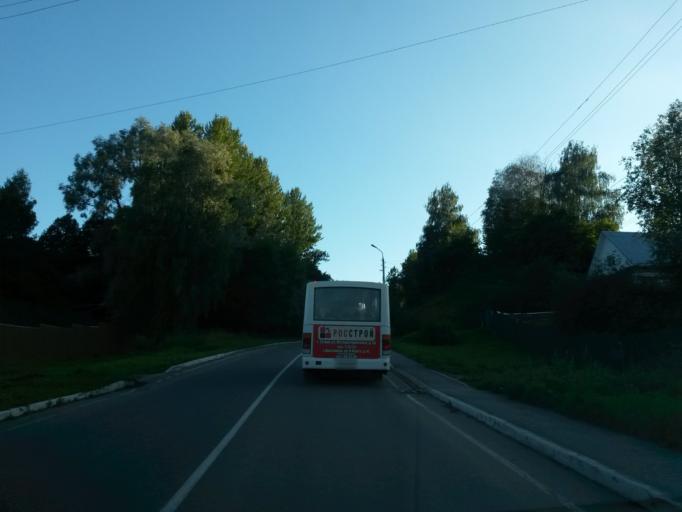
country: RU
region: Jaroslavl
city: Tutayev
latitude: 57.8715
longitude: 39.5384
